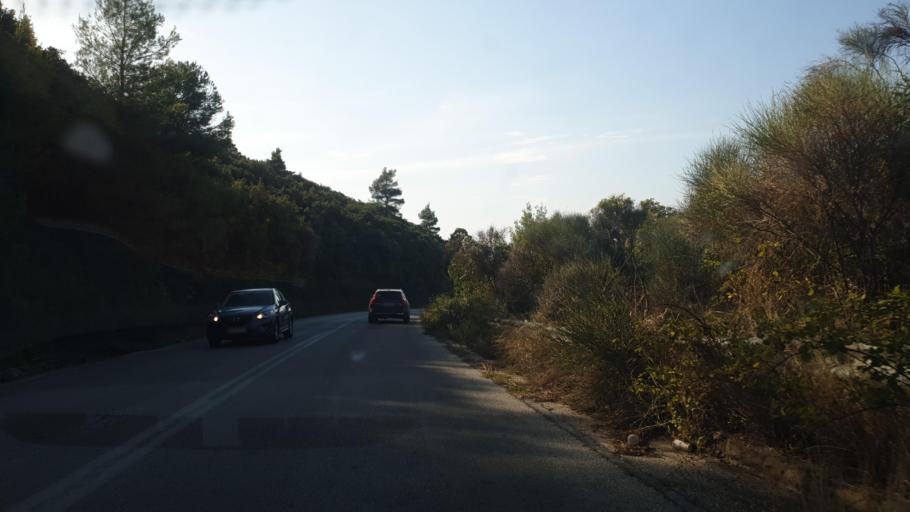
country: GR
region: Central Macedonia
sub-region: Nomos Chalkidikis
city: Neos Marmaras
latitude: 40.1670
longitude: 23.8637
